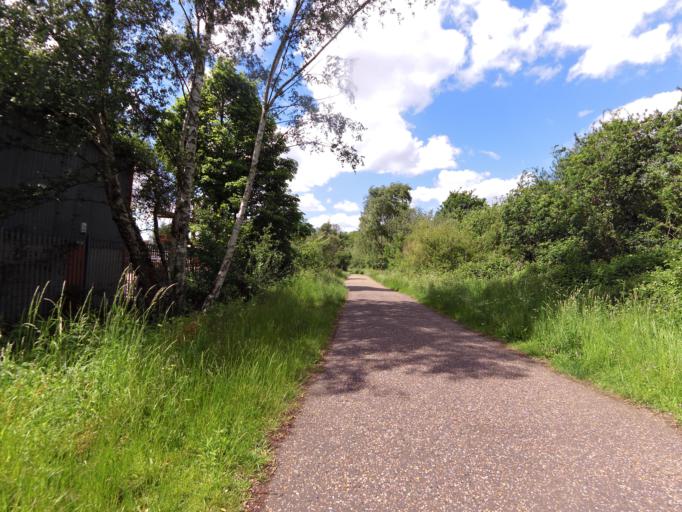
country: GB
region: England
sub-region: Norfolk
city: Norwich
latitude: 52.6395
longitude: 1.2848
